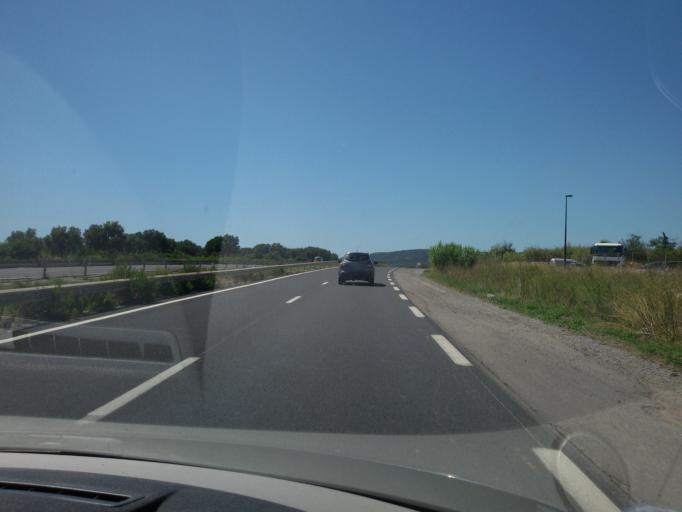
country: FR
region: Languedoc-Roussillon
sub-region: Departement de l'Herault
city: Mireval
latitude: 43.5227
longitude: 3.8141
